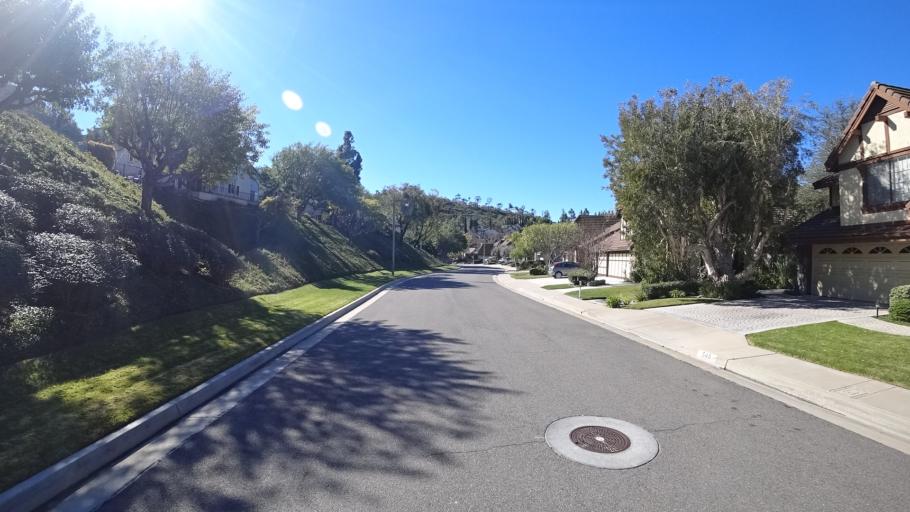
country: US
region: California
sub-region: Orange County
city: Villa Park
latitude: 33.8403
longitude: -117.8083
